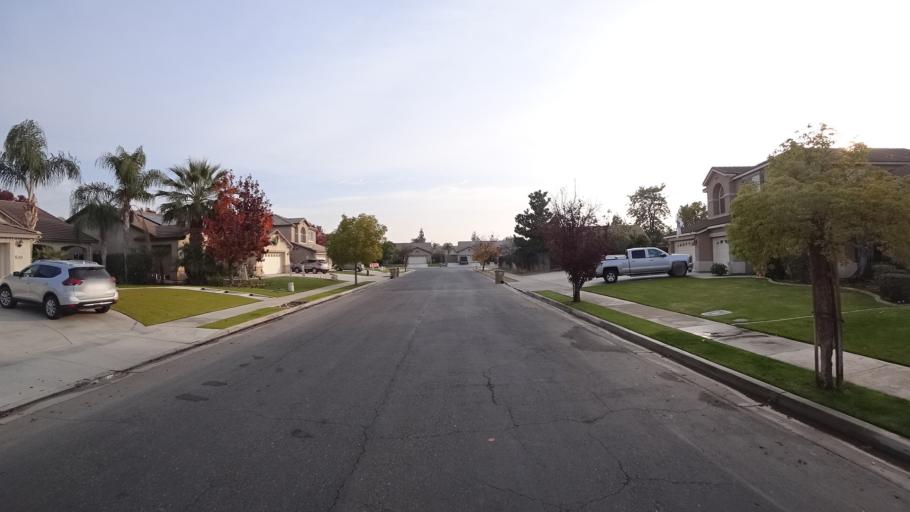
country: US
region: California
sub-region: Kern County
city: Greenacres
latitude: 35.4203
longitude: -119.1230
